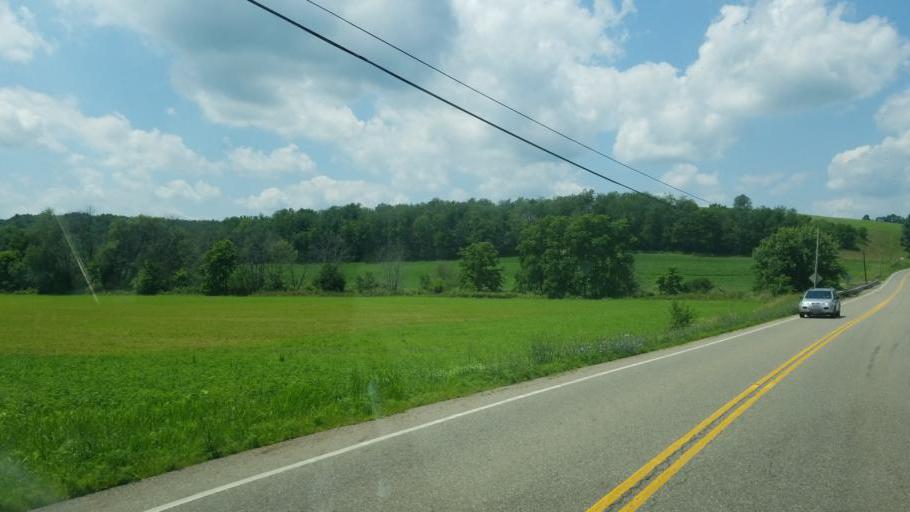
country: US
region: Ohio
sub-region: Stark County
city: Minerva
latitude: 40.7971
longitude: -81.1725
